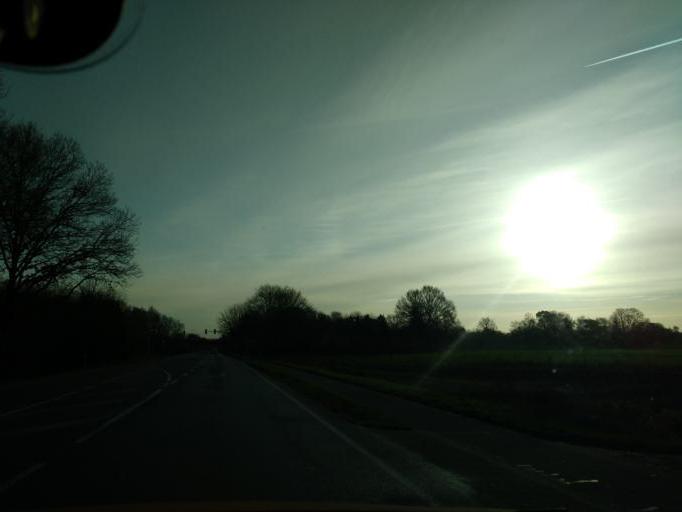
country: DE
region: Lower Saxony
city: Oldenburg
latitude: 53.1392
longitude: 8.2722
